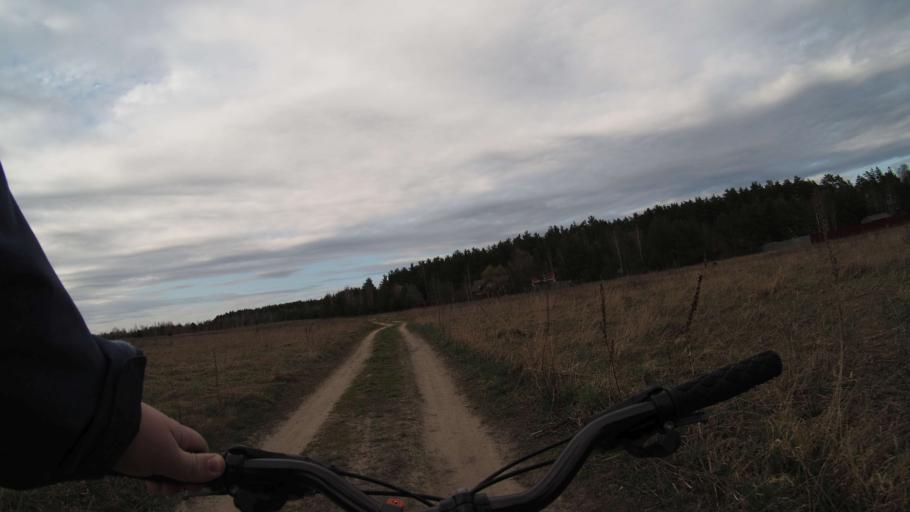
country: RU
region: Moskovskaya
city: Ramenskoye
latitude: 55.5893
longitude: 38.2894
